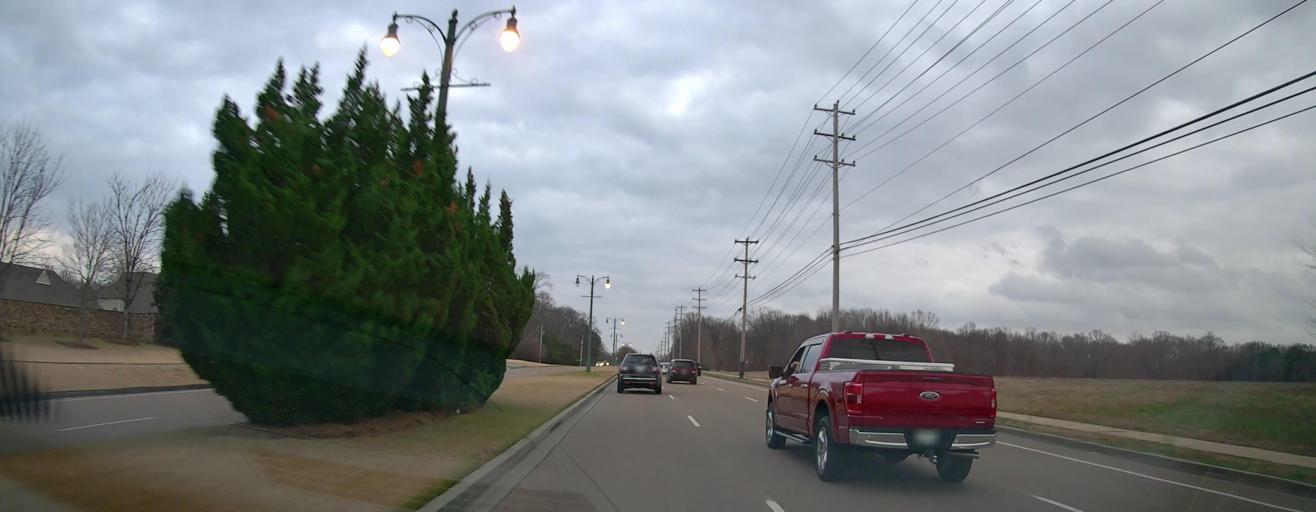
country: US
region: Tennessee
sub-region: Shelby County
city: Germantown
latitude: 35.0475
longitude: -89.7529
